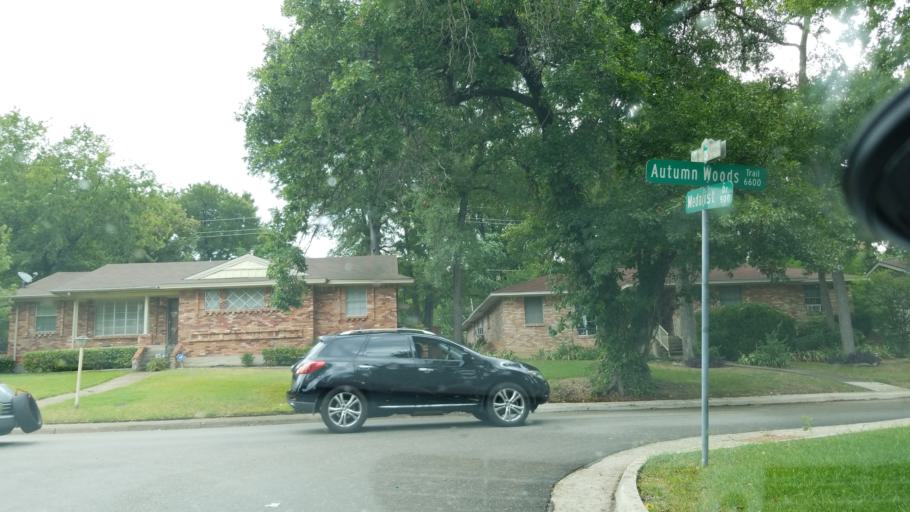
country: US
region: Texas
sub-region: Dallas County
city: Duncanville
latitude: 32.6678
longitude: -96.8363
